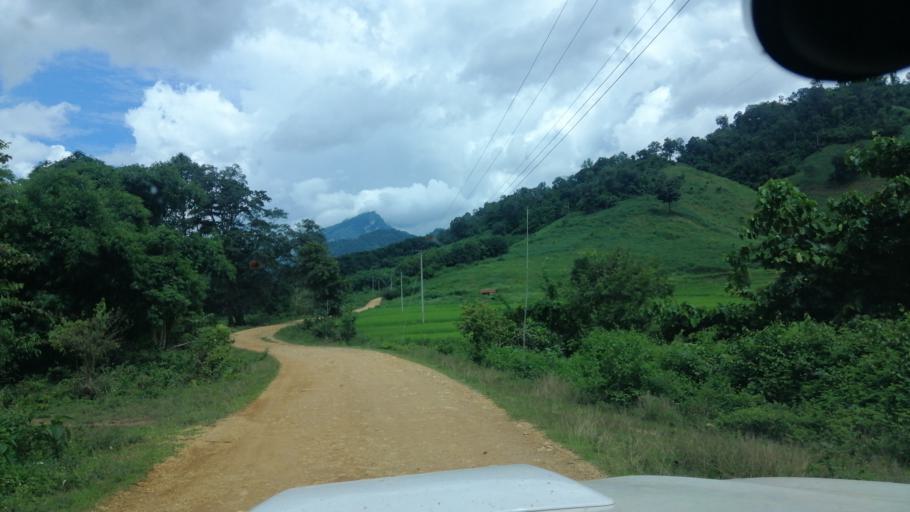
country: TH
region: Phayao
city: Phu Sang
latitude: 19.7155
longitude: 100.4881
